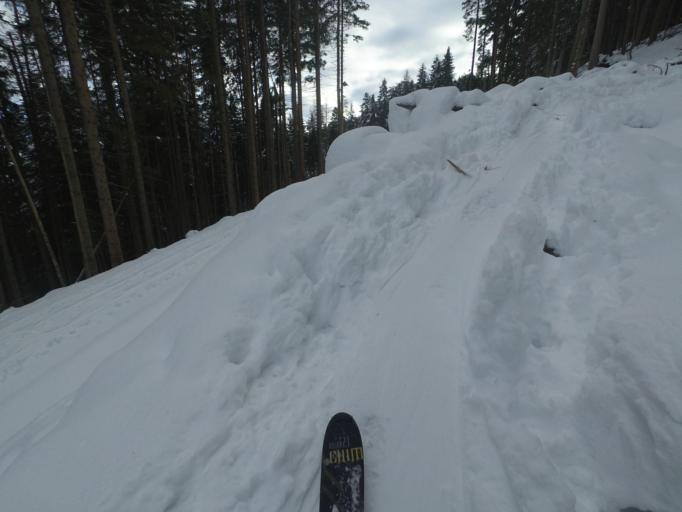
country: AT
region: Salzburg
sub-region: Politischer Bezirk Sankt Johann im Pongau
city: Sankt Johann im Pongau
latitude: 47.3226
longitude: 13.2181
